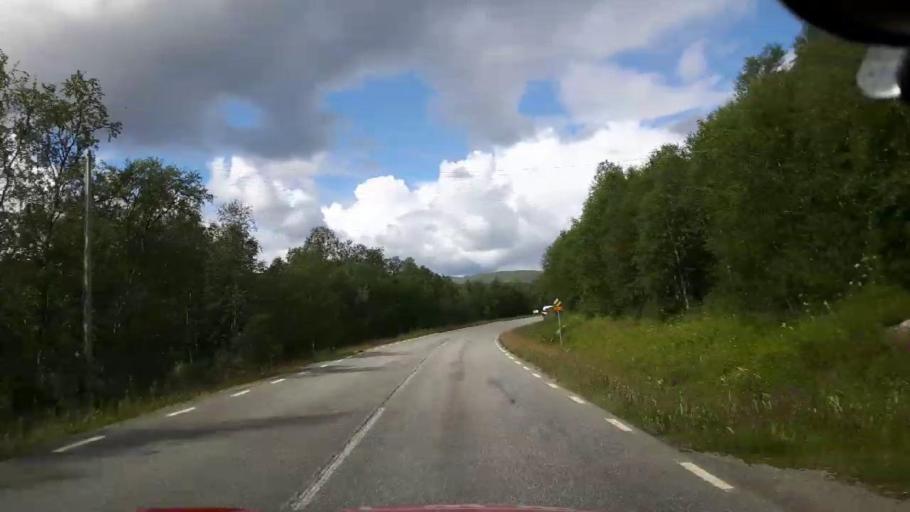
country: NO
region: Nordland
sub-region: Hattfjelldal
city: Hattfjelldal
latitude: 65.0506
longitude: 14.7463
